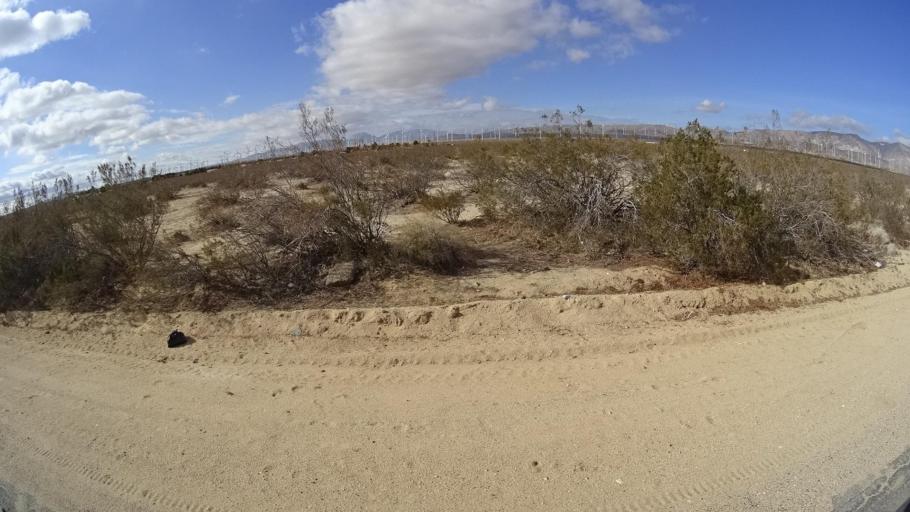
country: US
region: California
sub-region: Kern County
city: Mojave
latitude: 35.0642
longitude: -118.1859
